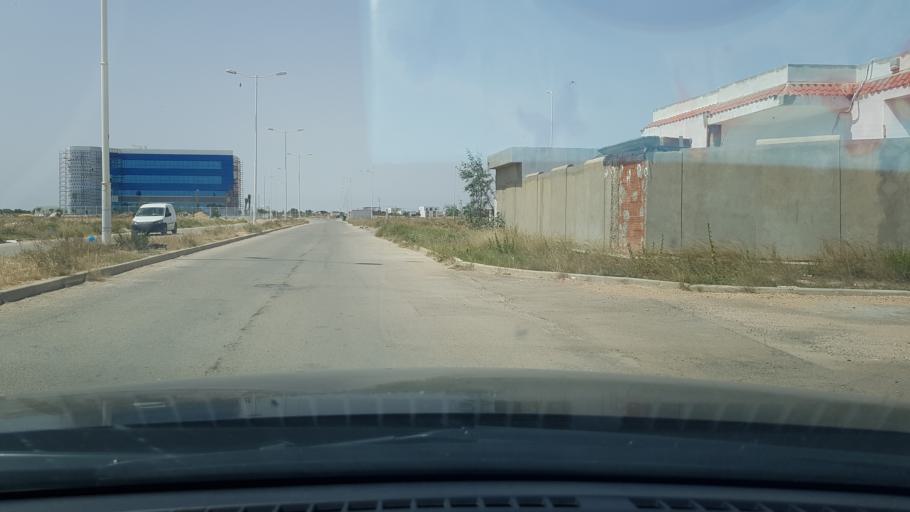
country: TN
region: Safaqis
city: Al Qarmadah
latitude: 34.8309
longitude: 10.7487
